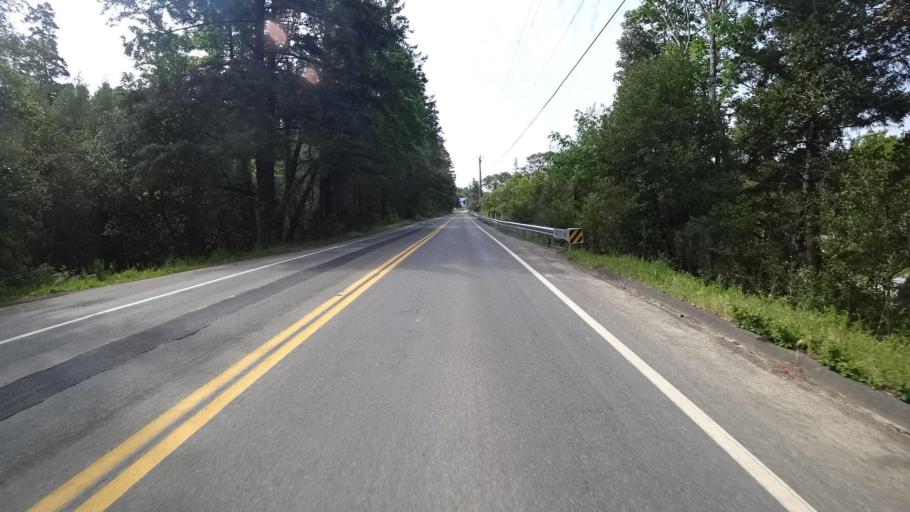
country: US
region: California
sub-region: Humboldt County
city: Redway
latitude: 40.1125
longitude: -123.7945
